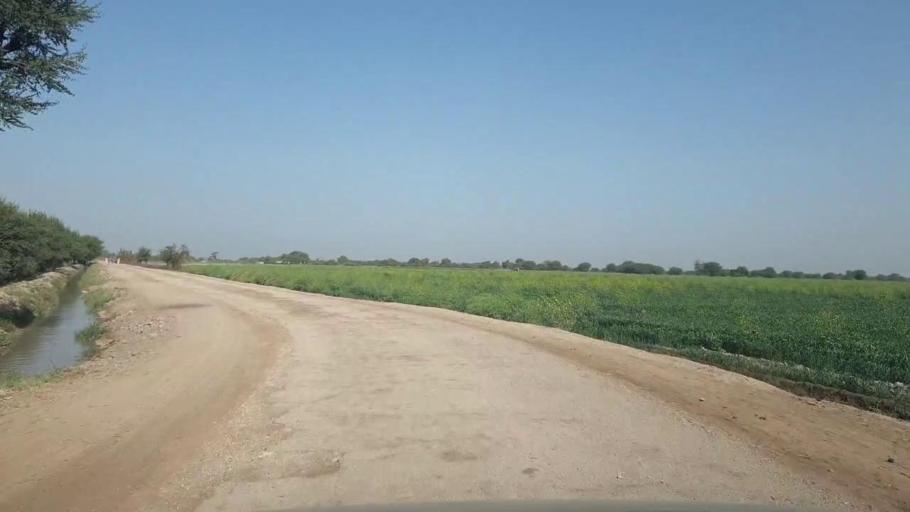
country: PK
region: Sindh
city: Umarkot
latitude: 25.2952
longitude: 69.6579
